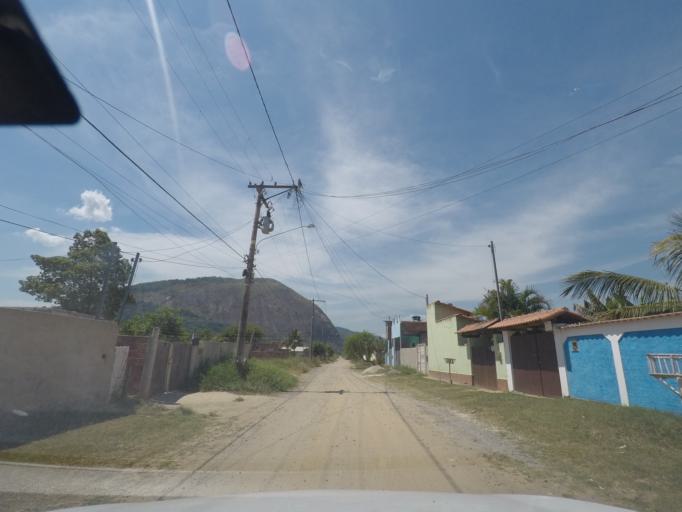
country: BR
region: Rio de Janeiro
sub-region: Marica
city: Marica
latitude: -22.9536
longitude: -42.9577
